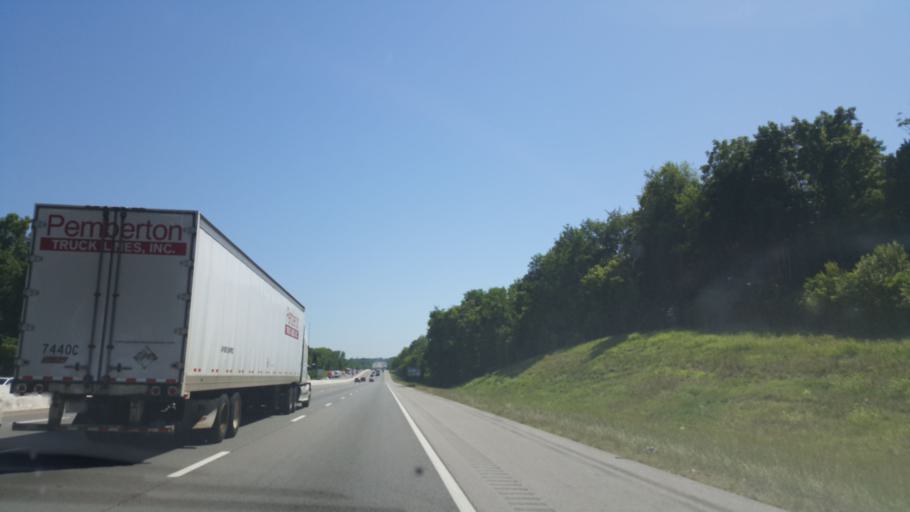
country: US
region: Tennessee
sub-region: Davidson County
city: Lakewood
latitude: 36.1482
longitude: -86.6411
